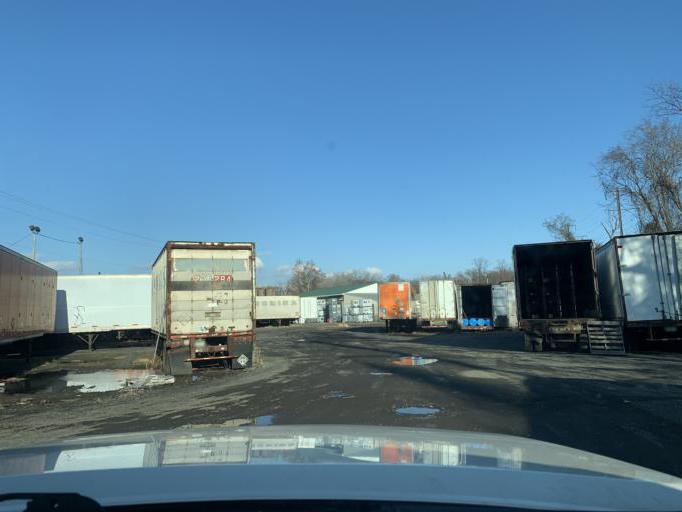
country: US
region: Maryland
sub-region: Prince George's County
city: Fairmount Heights
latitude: 38.9130
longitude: -76.9274
